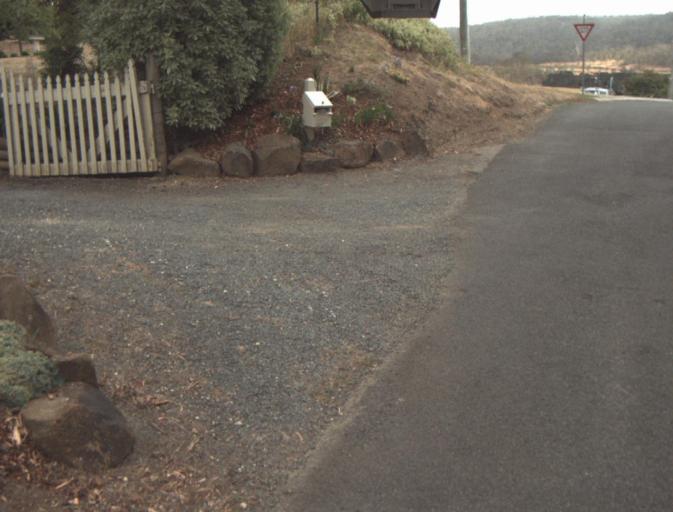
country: AU
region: Tasmania
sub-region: Launceston
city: Mayfield
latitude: -41.3295
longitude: 147.0673
